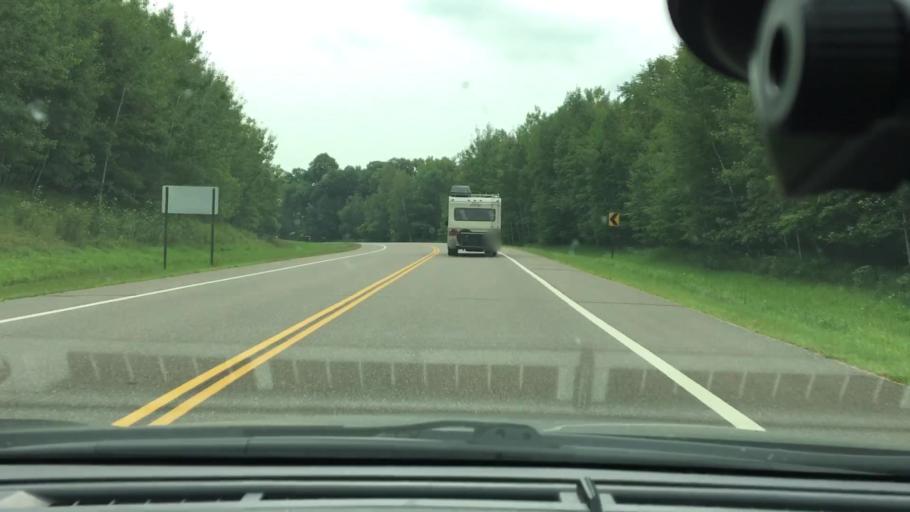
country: US
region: Minnesota
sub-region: Crow Wing County
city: Crosby
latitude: 46.4094
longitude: -93.8234
